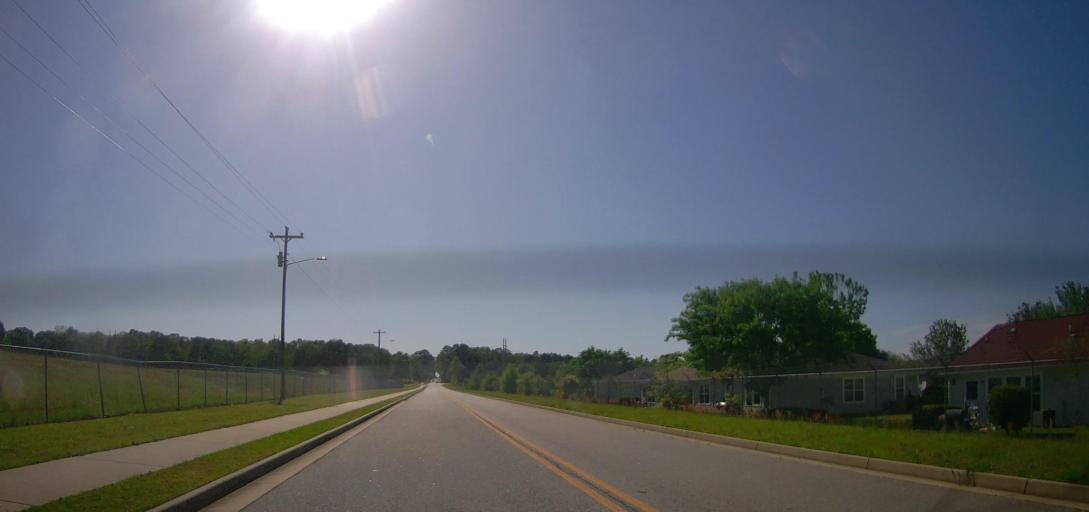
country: US
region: Georgia
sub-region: Houston County
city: Robins Air Force Base
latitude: 32.6017
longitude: -83.5987
